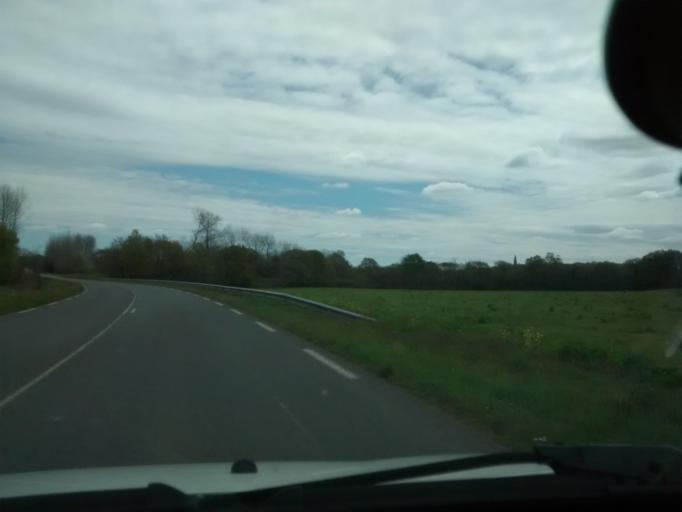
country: FR
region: Brittany
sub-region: Departement des Cotes-d'Armor
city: Langoat
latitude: 48.7578
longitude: -3.2896
